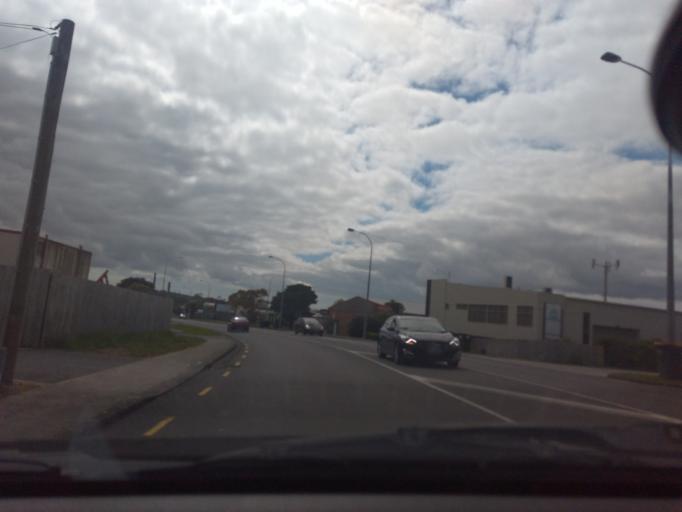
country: NZ
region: Auckland
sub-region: Auckland
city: Rosebank
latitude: -36.8654
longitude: 174.5863
